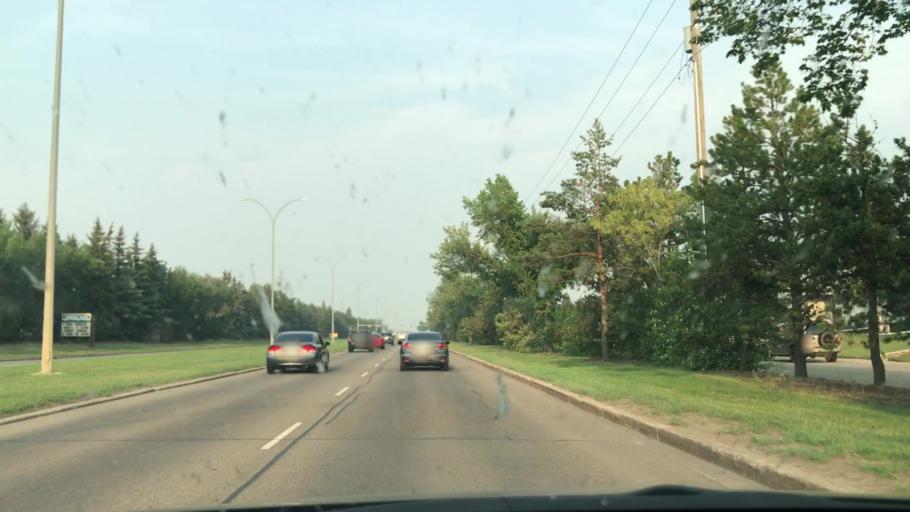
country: CA
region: Alberta
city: Edmonton
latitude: 53.5996
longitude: -113.4617
